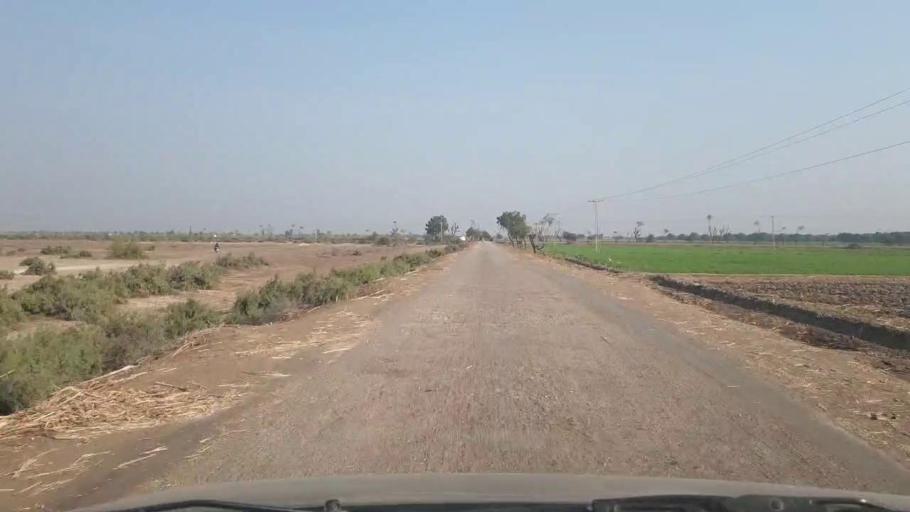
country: PK
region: Sindh
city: Digri
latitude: 25.2374
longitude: 69.1960
